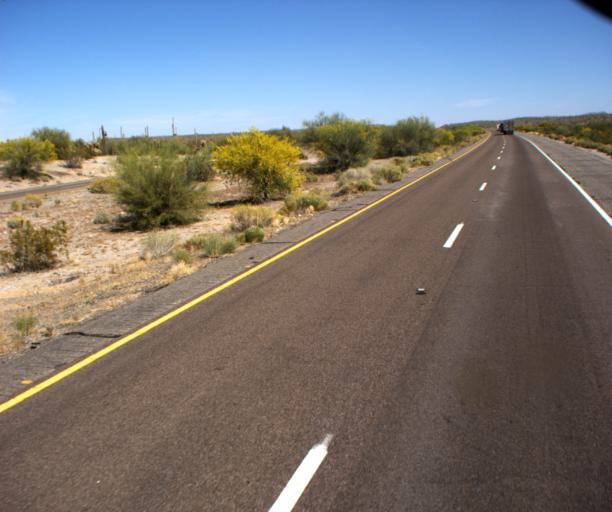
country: US
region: Arizona
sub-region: Maricopa County
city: Gila Bend
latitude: 32.8510
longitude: -112.3586
